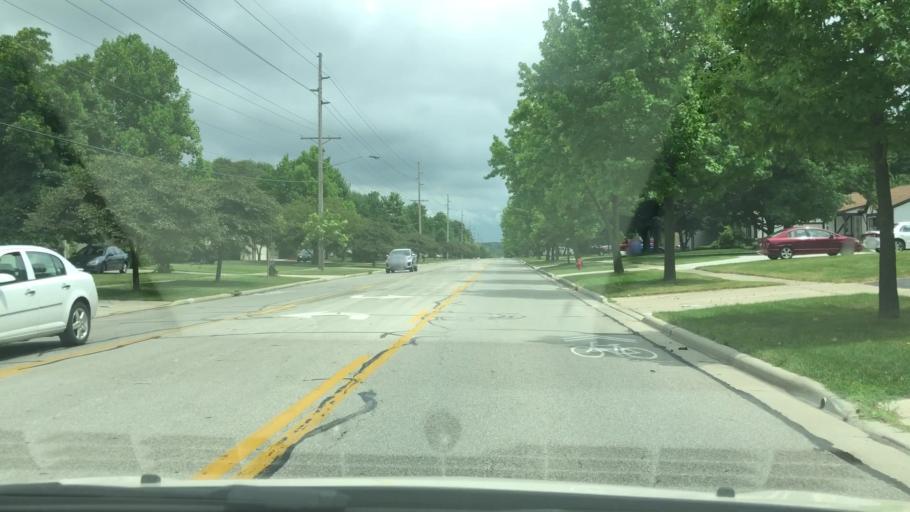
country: US
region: Ohio
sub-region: Franklin County
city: Westerville
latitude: 40.1251
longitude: -82.9593
